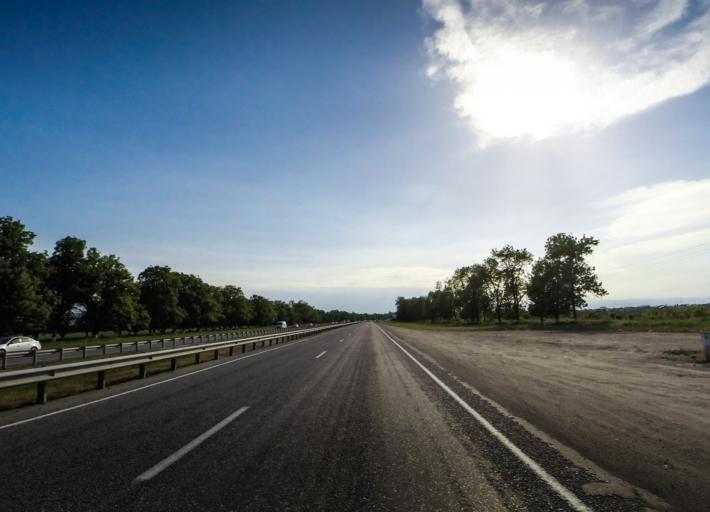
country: RU
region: Kabardino-Balkariya
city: Nartan
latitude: 43.4894
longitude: 43.6822
